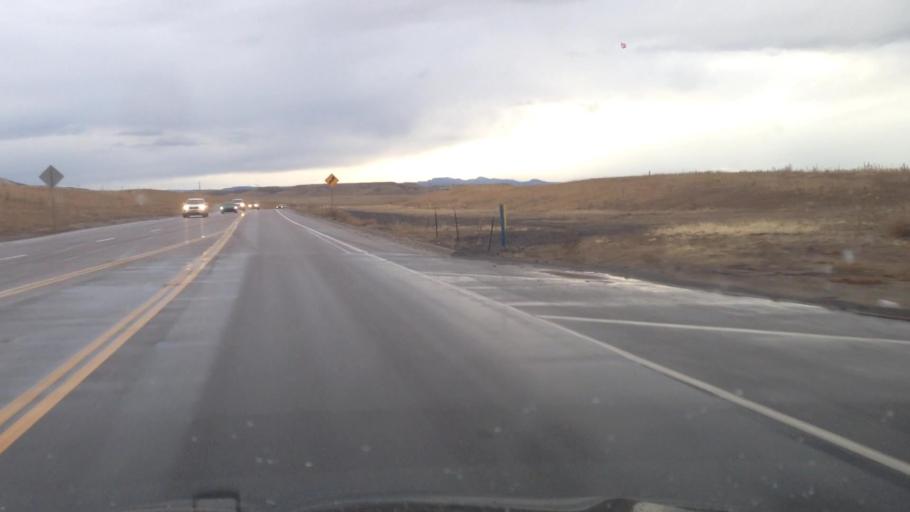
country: US
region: Colorado
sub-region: Douglas County
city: Stonegate
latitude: 39.5200
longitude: -104.8298
